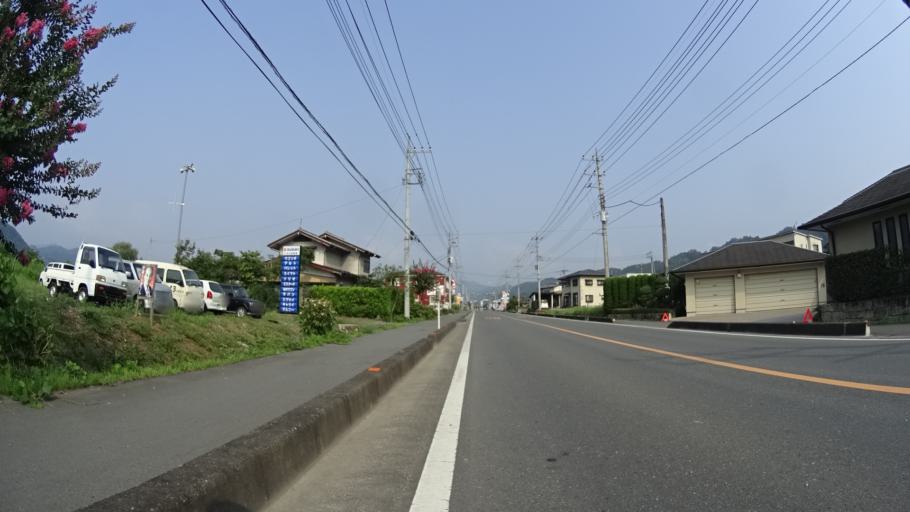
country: JP
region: Saitama
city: Chichibu
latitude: 36.0207
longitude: 139.0089
